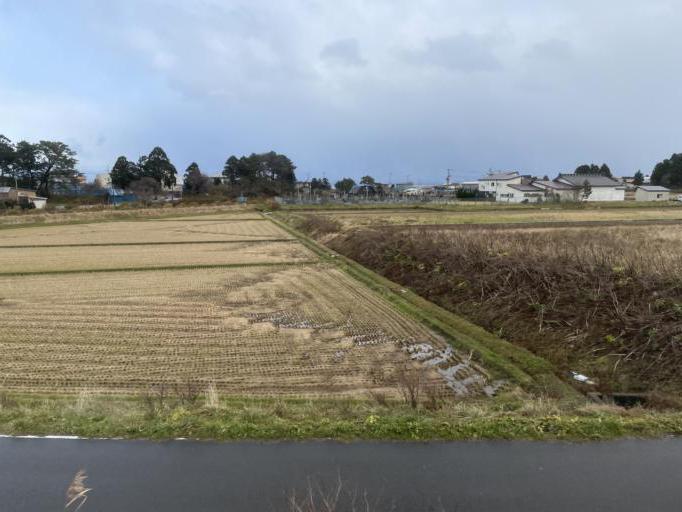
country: JP
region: Aomori
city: Aomori Shi
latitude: 41.0162
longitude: 140.6449
